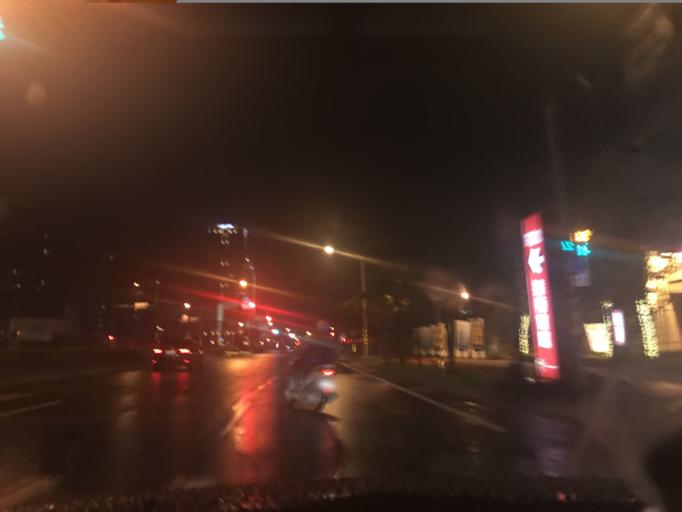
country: TW
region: Taiwan
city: Daxi
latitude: 24.9310
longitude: 121.2810
